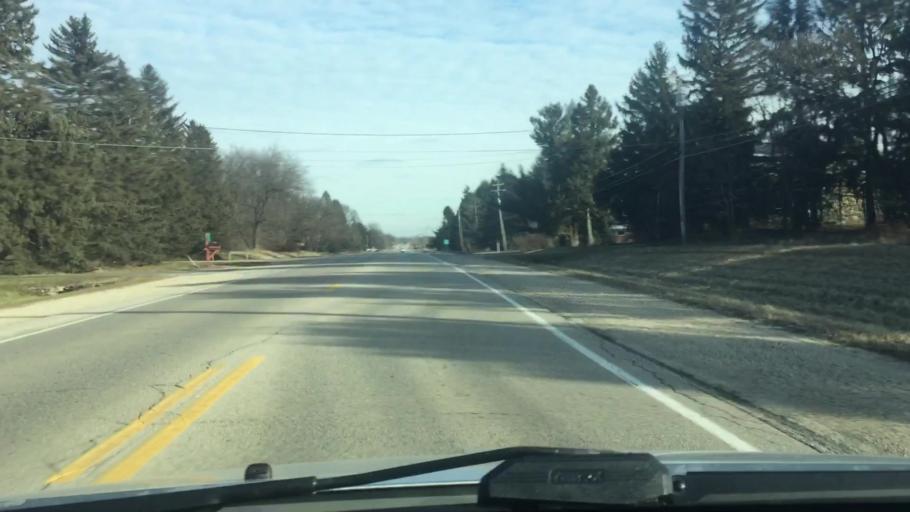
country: US
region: Wisconsin
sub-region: Waukesha County
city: Sussex
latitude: 43.1120
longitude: -88.2304
